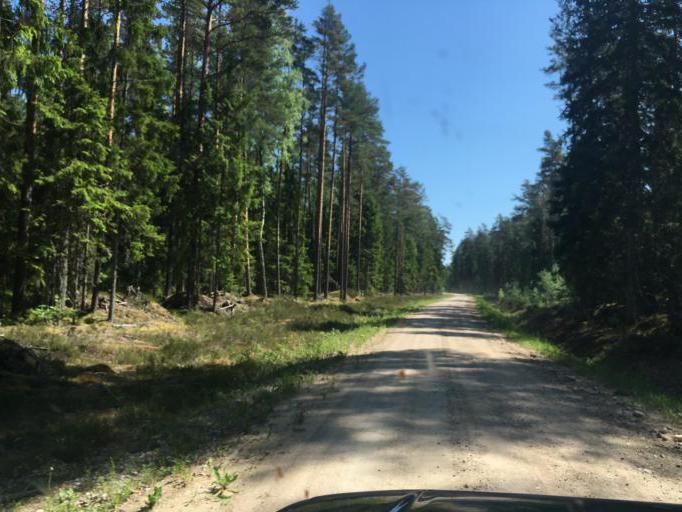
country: LV
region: Talsu Rajons
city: Valdemarpils
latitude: 57.4333
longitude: 22.6892
